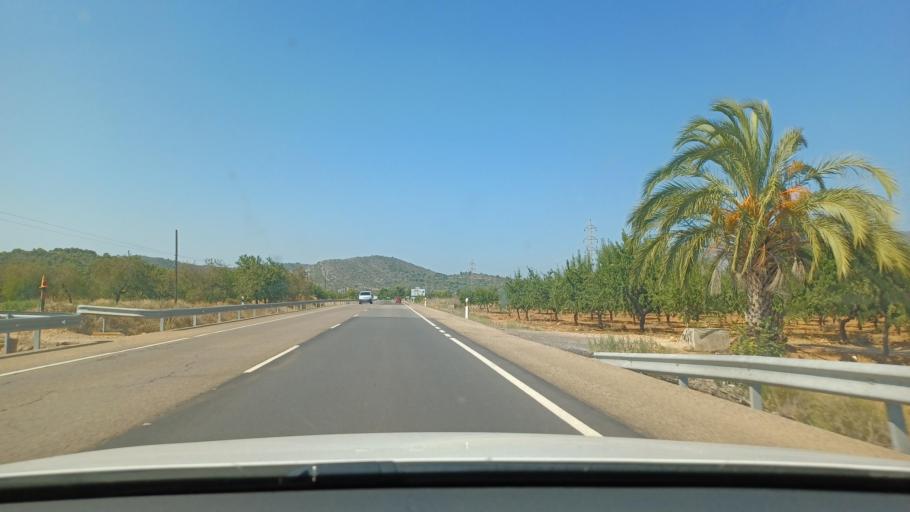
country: ES
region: Valencia
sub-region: Provincia de Castello
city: Alcala de Xivert
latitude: 40.2601
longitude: 0.2382
